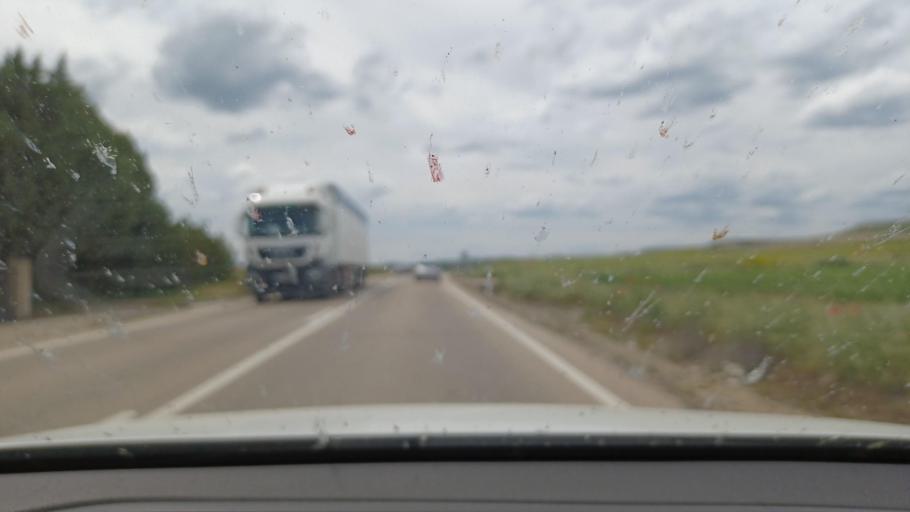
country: ES
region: Castille and Leon
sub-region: Provincia de Segovia
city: Cuellar
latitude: 41.3851
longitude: -4.2590
